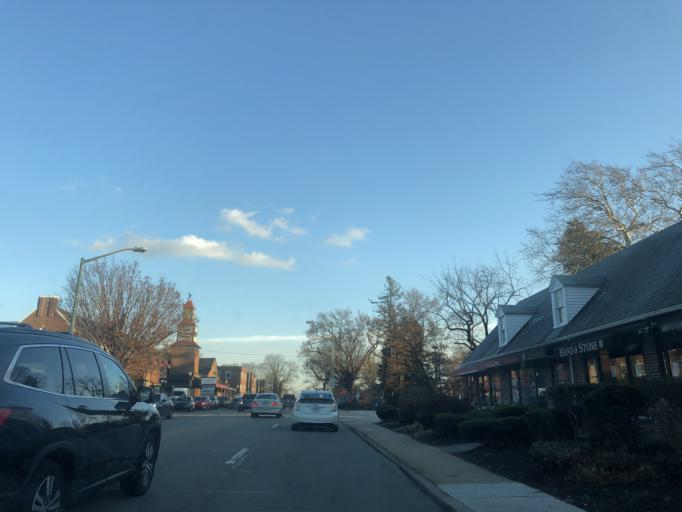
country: US
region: Pennsylvania
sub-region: Montgomery County
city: Bryn Mawr
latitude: 40.0131
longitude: -75.3014
